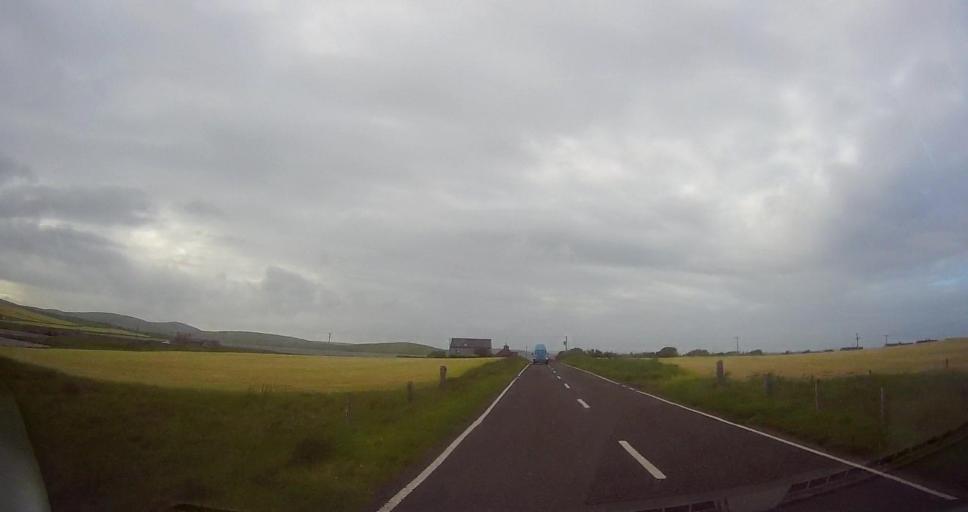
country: GB
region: Scotland
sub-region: Orkney Islands
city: Stromness
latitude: 58.9810
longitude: -3.2456
